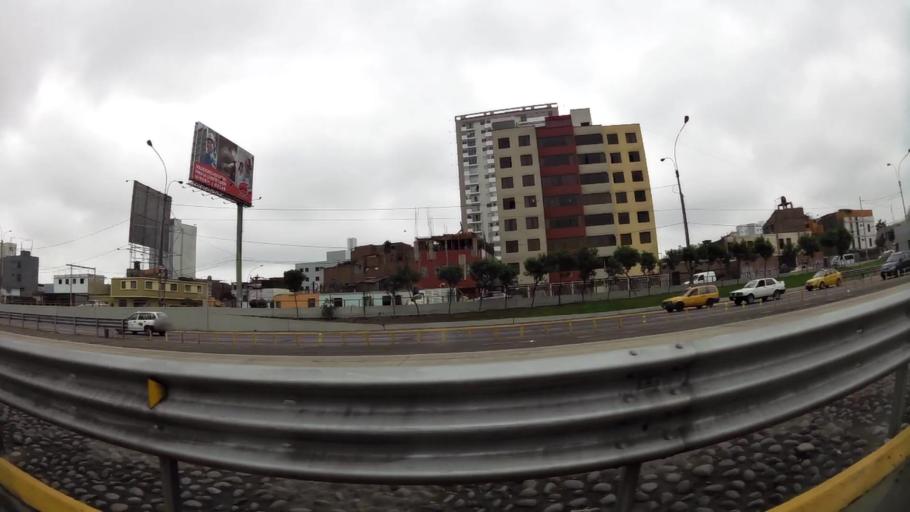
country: PE
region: Lima
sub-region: Lima
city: San Luis
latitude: -12.0792
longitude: -77.0277
